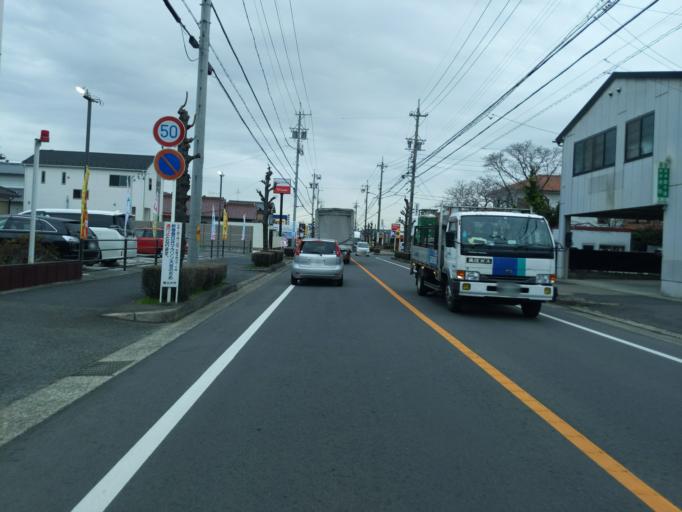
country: JP
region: Aichi
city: Kasugai
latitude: 35.2594
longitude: 136.9534
